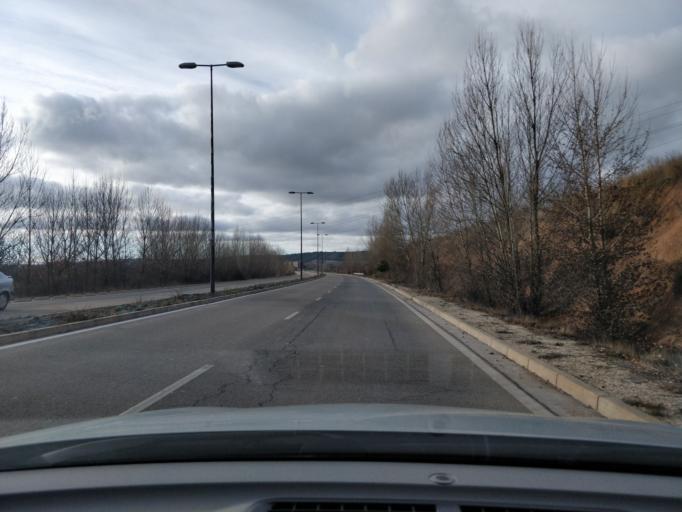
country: ES
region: Castille and Leon
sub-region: Provincia de Burgos
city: Villalbilla de Burgos
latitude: 42.3536
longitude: -3.7471
